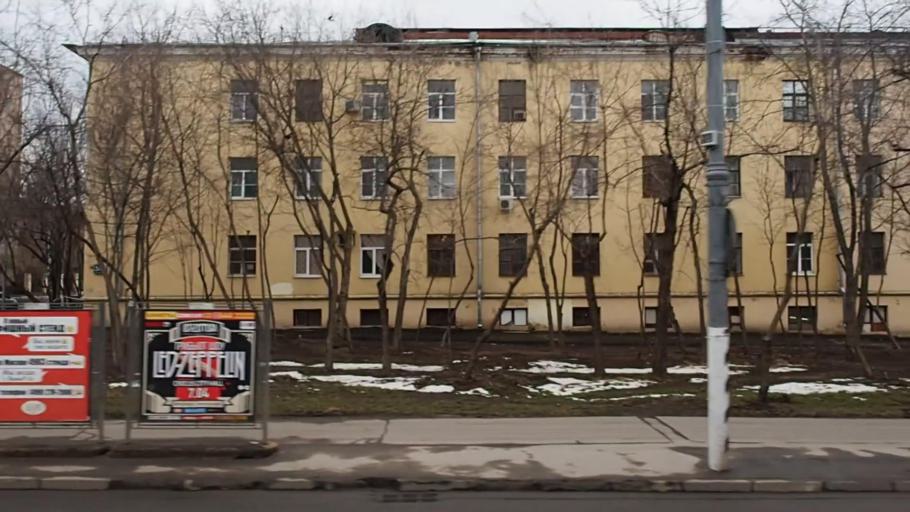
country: RU
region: Moskovskaya
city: Leninskiye Gory
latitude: 55.6973
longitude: 37.5714
